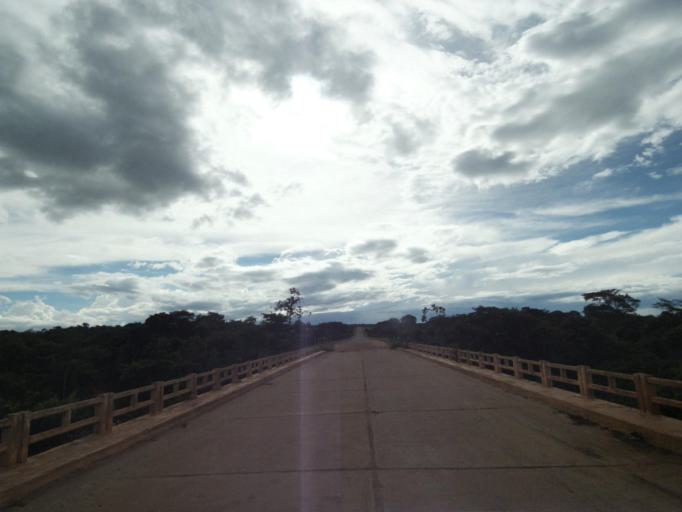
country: BR
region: Goias
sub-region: Jaragua
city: Jaragua
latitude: -15.8424
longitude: -49.3455
